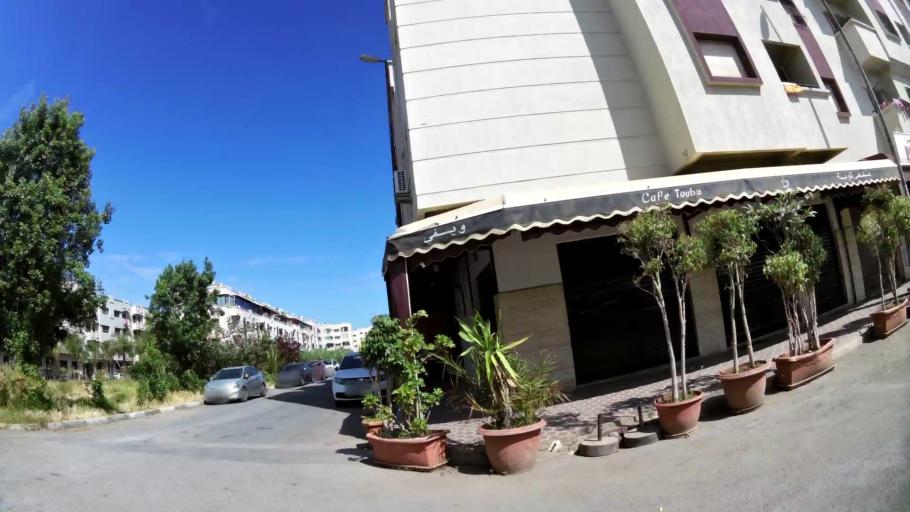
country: MA
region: Rabat-Sale-Zemmour-Zaer
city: Sale
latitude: 34.0631
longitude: -6.7991
